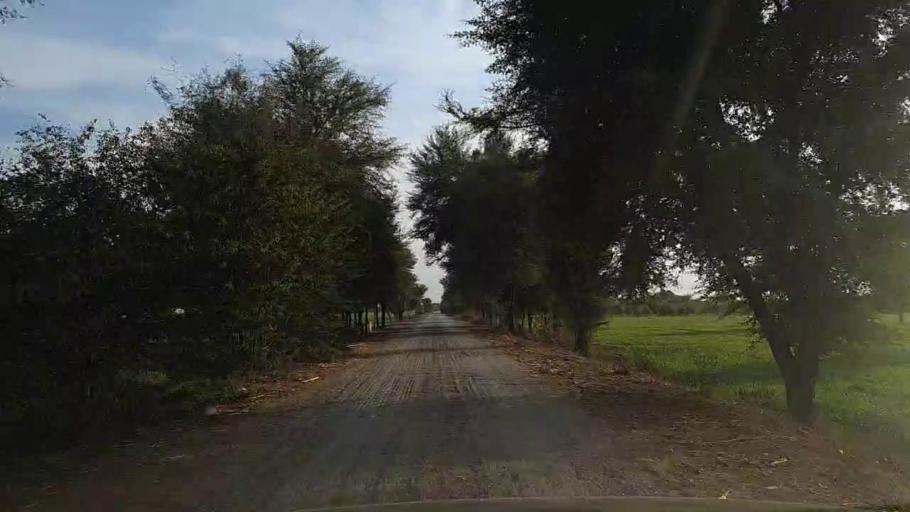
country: PK
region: Sindh
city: Jam Sahib
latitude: 26.4365
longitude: 68.5716
